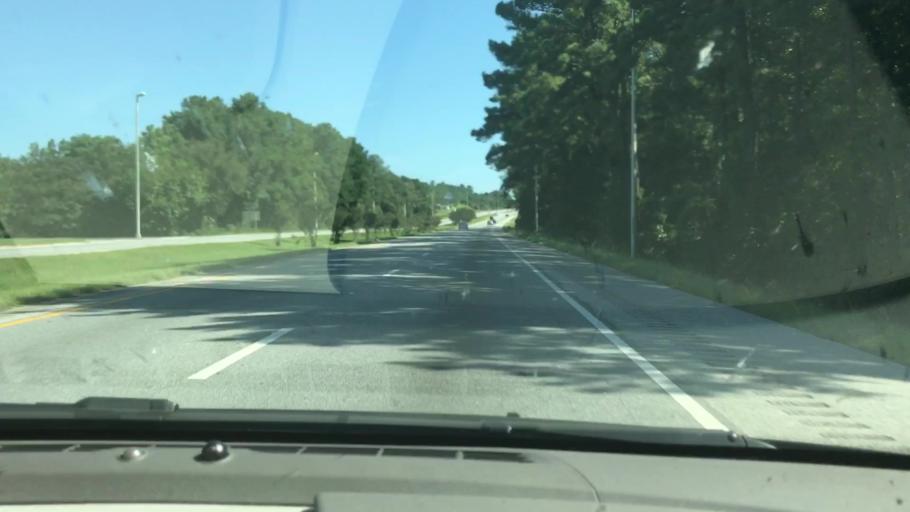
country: US
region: Alabama
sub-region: Russell County
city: Phenix City
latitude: 32.4433
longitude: -85.0199
